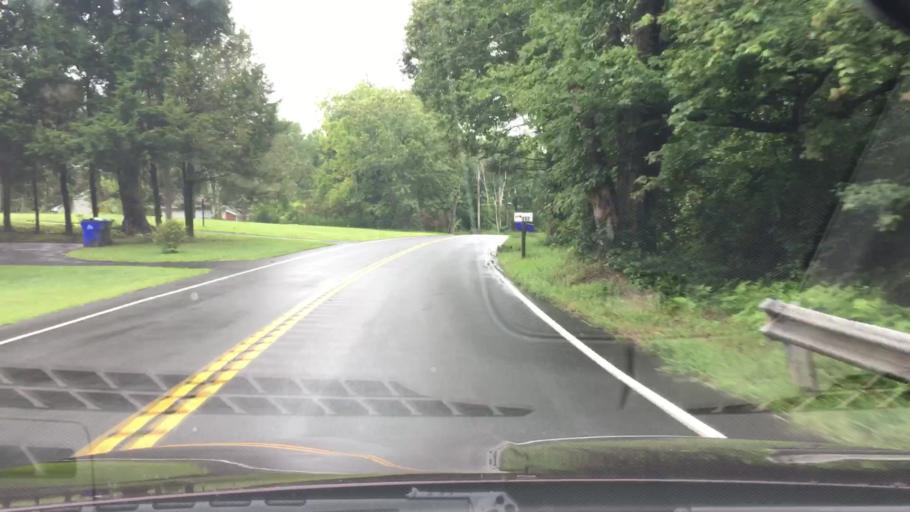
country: US
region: Connecticut
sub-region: Hartford County
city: Tariffville
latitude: 41.9335
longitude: -72.7522
